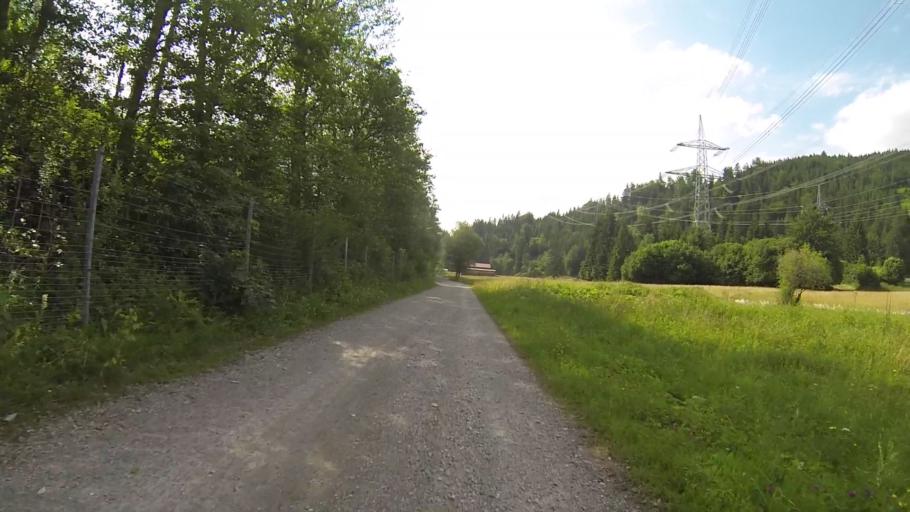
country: AT
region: Tyrol
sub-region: Politischer Bezirk Reutte
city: Pflach
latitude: 47.5198
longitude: 10.7218
